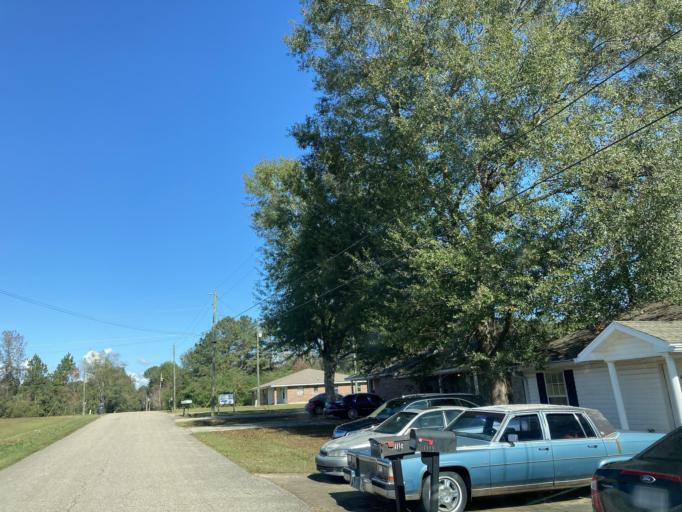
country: US
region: Mississippi
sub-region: Lamar County
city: West Hattiesburg
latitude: 31.2596
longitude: -89.4220
